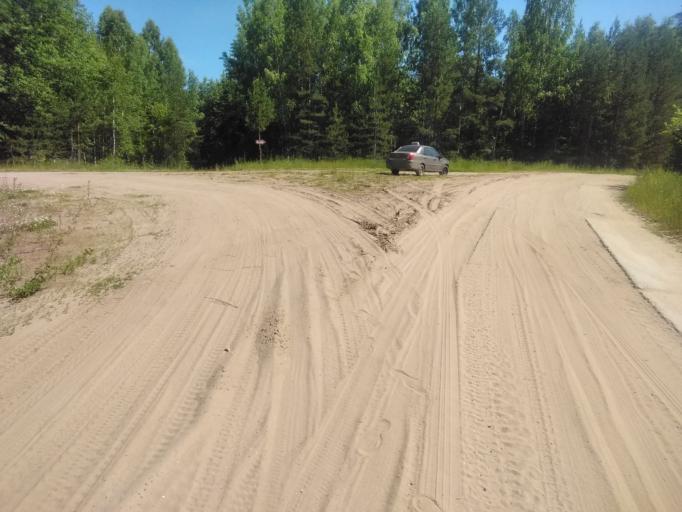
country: RU
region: Perm
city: Foki
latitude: 56.5119
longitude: 54.5774
